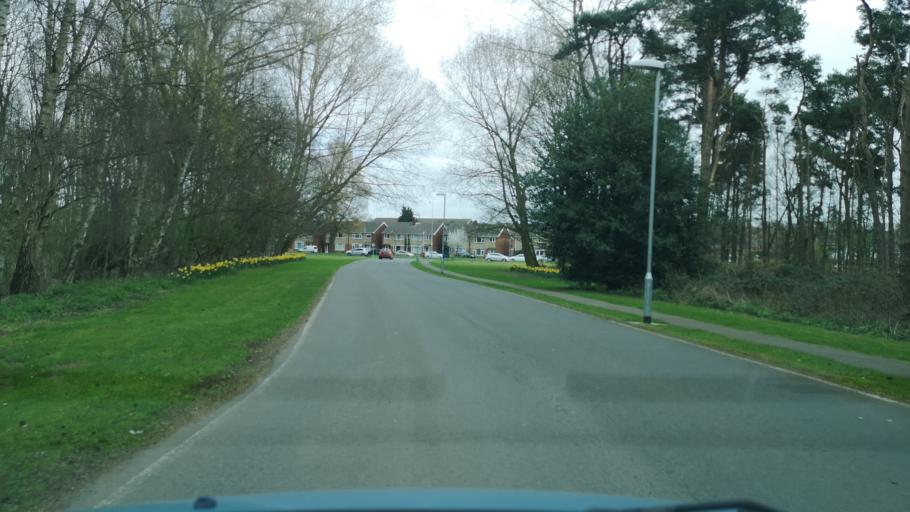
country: GB
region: England
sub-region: North Lincolnshire
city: Scunthorpe
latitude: 53.5698
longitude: -0.6843
